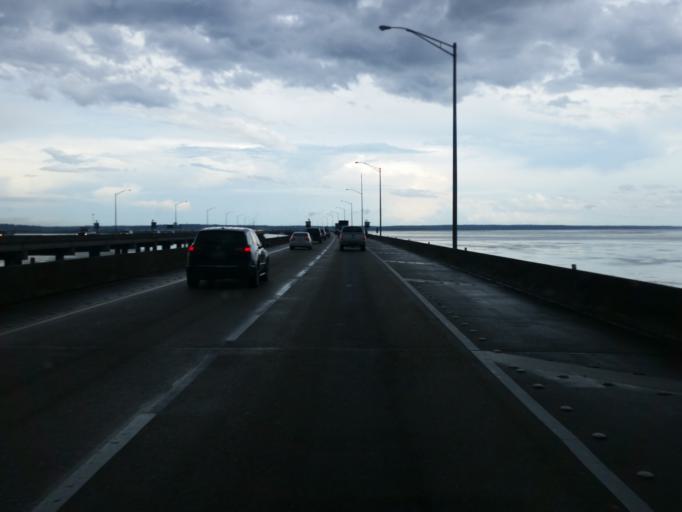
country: US
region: Alabama
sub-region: Baldwin County
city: Spanish Fort
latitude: 30.6724
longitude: -87.9796
